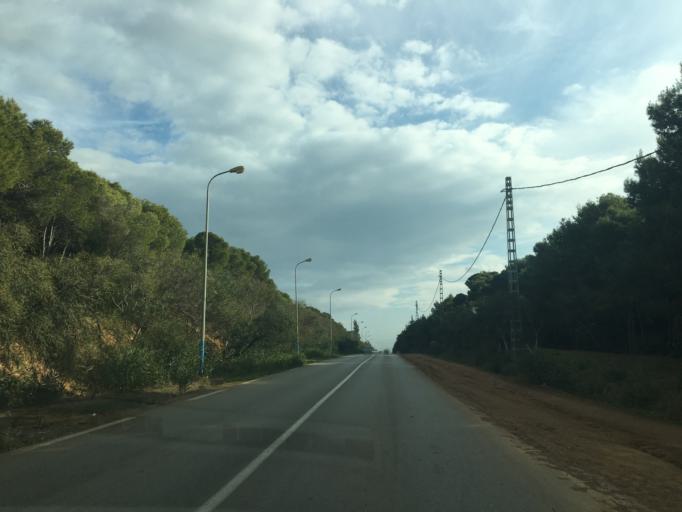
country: DZ
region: Tipaza
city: Tipasa
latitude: 36.5886
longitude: 2.4747
